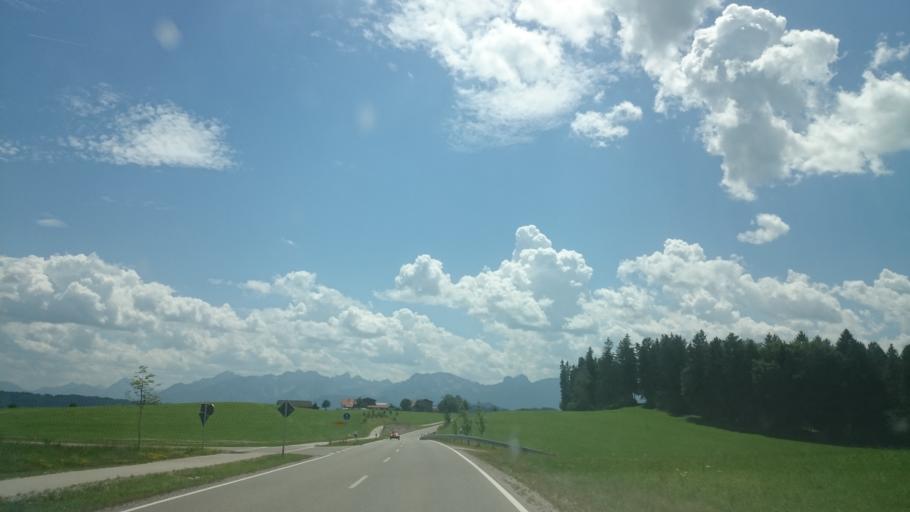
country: DE
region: Bavaria
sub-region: Swabia
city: Lengenwang
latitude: 47.6858
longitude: 10.6051
